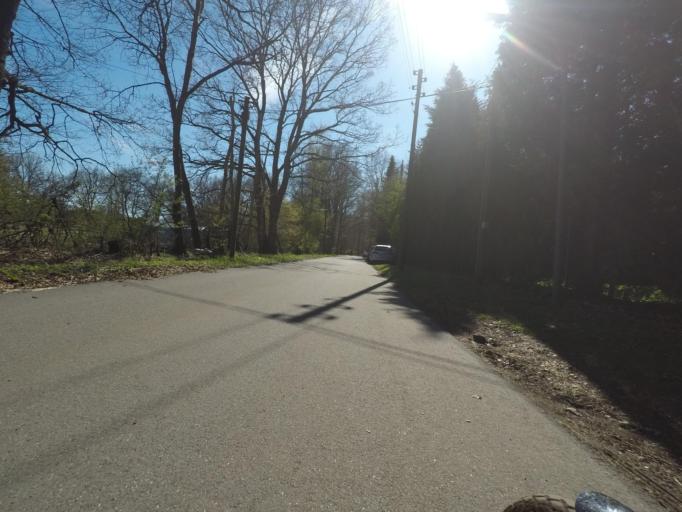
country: DE
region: Hamburg
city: Langenhorn
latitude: 53.6478
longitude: 9.9733
